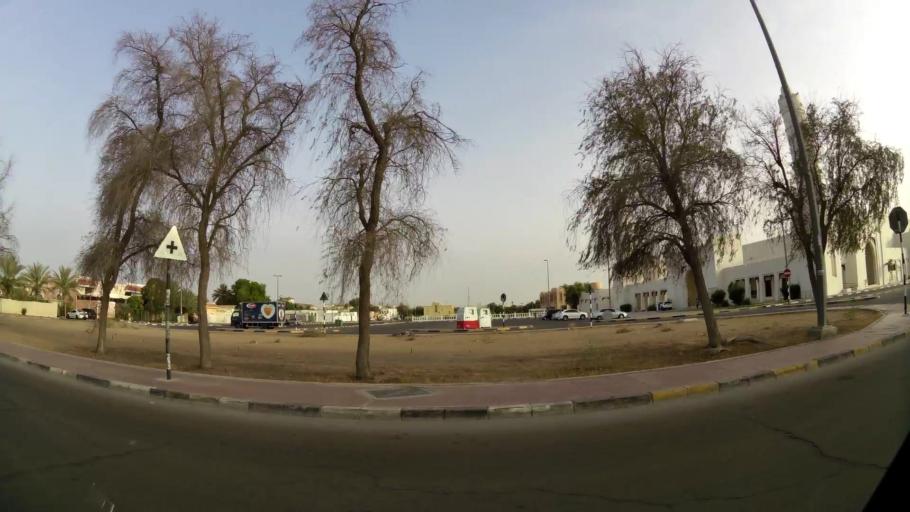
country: OM
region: Al Buraimi
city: Al Buraymi
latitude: 24.2456
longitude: 55.7411
